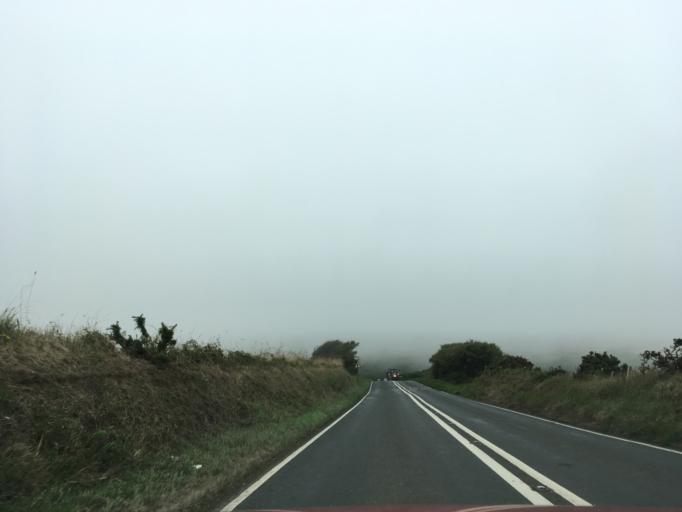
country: GB
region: Wales
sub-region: Pembrokeshire
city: Saint David's
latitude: 51.8800
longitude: -5.2389
